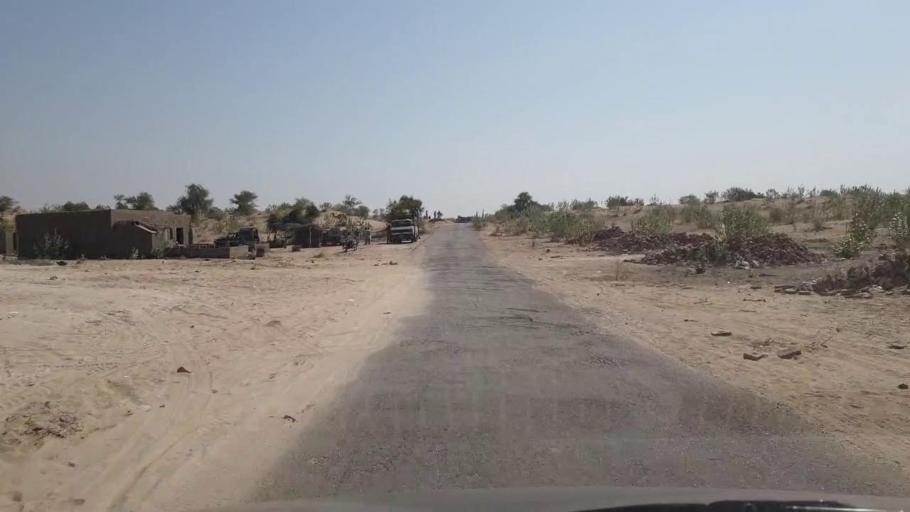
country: PK
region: Sindh
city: Chor
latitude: 25.6005
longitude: 70.0020
